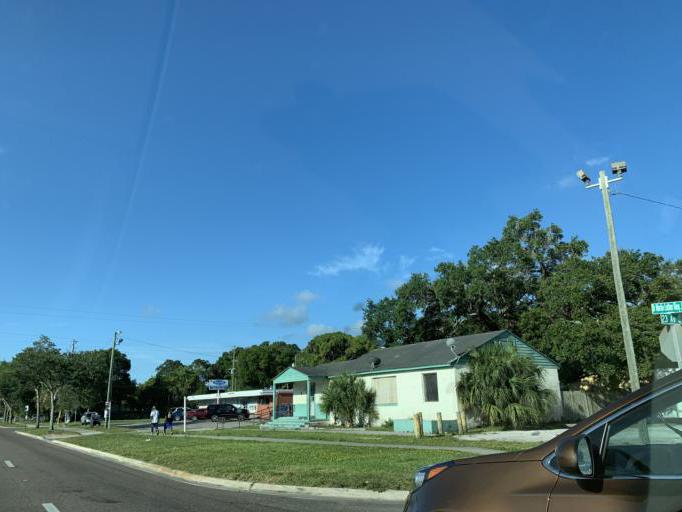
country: US
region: Florida
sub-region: Pinellas County
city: Saint Petersburg
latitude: 27.7475
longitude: -82.6466
